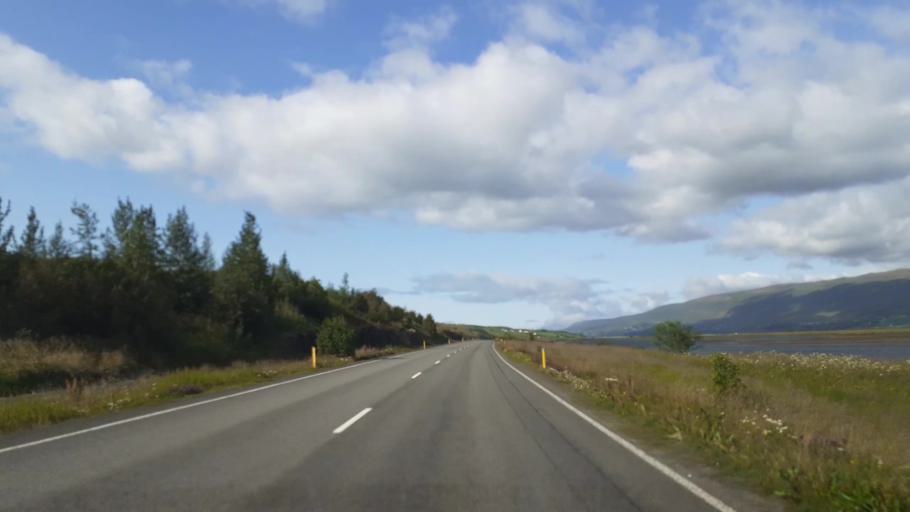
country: IS
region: Northeast
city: Akureyri
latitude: 65.6064
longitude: -18.0807
